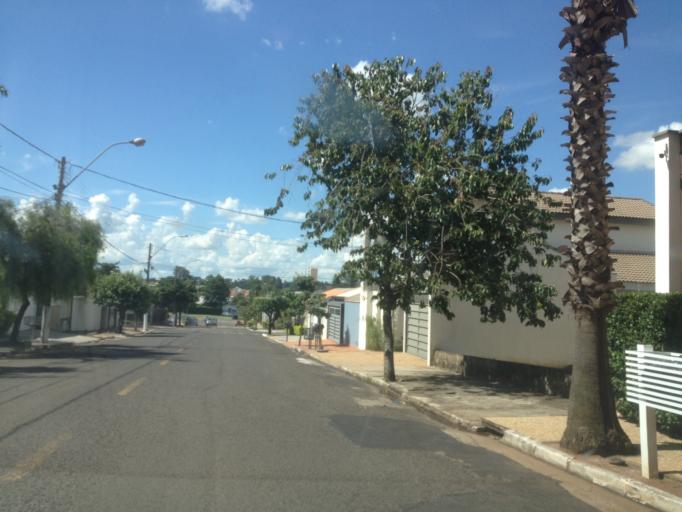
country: BR
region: Sao Paulo
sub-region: Marilia
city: Marilia
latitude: -22.2247
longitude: -49.9323
